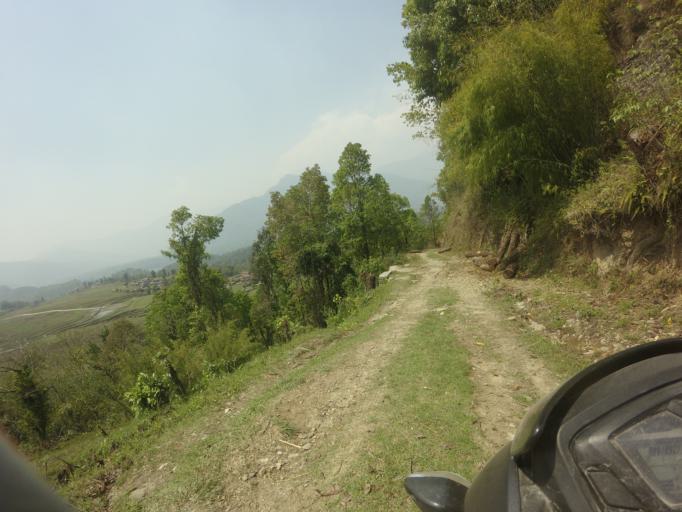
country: NP
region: Western Region
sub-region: Gandaki Zone
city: Pokhara
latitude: 28.3022
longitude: 83.9655
